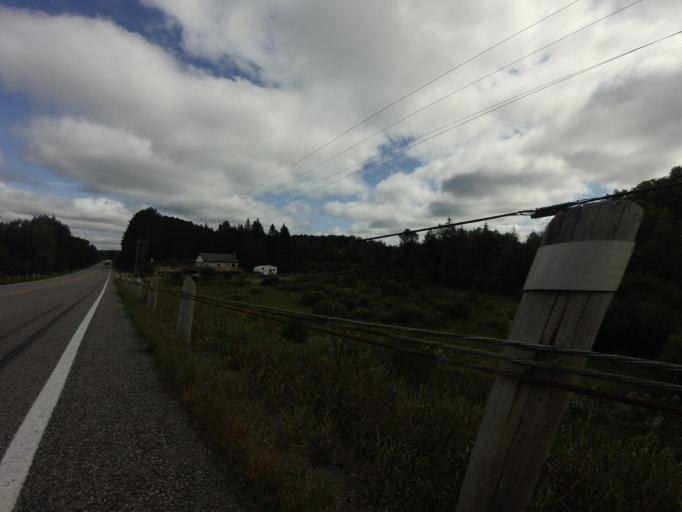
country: CA
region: Ontario
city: Omemee
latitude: 44.8178
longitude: -78.5718
